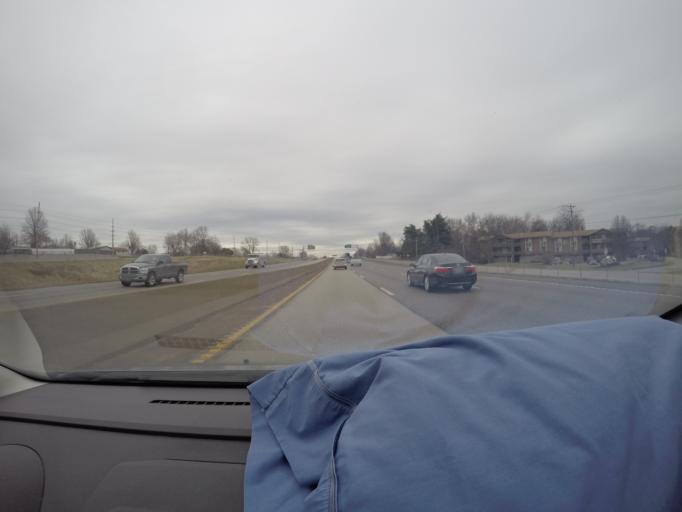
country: US
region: Missouri
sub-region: Saint Charles County
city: Saint Charles
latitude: 38.7891
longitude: -90.5462
